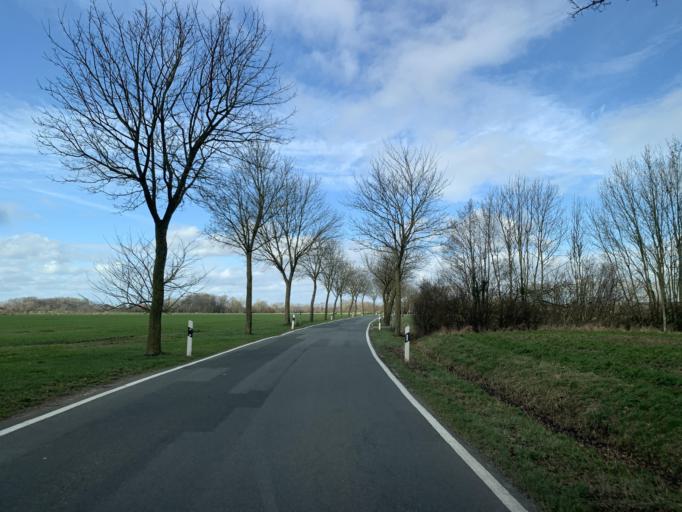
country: DE
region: North Rhine-Westphalia
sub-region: Regierungsbezirk Munster
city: Havixbeck
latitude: 52.0164
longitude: 7.4041
